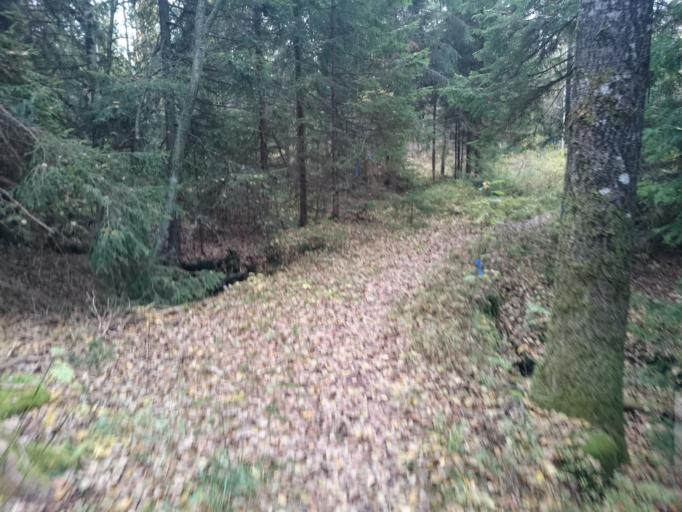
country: SE
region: OErebro
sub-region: Laxa Kommun
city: Laxa
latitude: 58.7625
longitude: 14.5932
